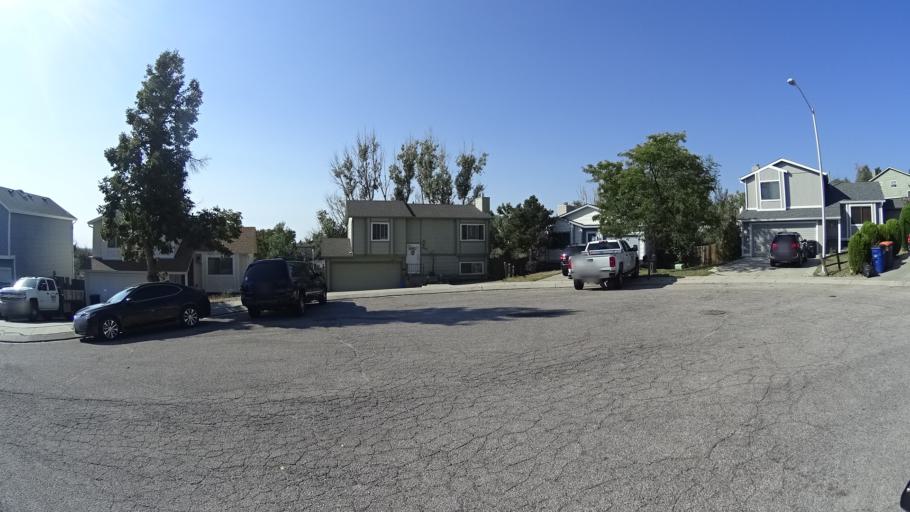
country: US
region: Colorado
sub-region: El Paso County
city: Cimarron Hills
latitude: 38.8896
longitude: -104.7242
